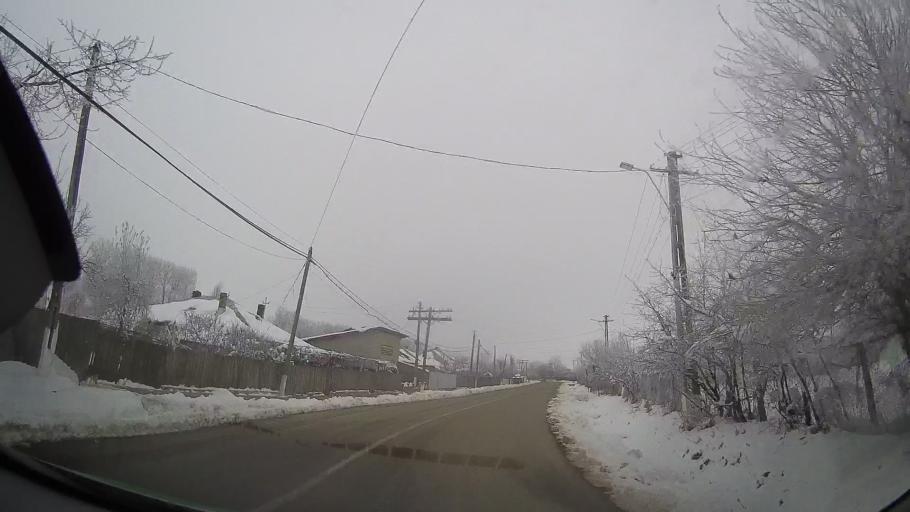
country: RO
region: Iasi
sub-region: Comuna Dagata
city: Dagata
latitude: 46.9167
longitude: 27.2036
